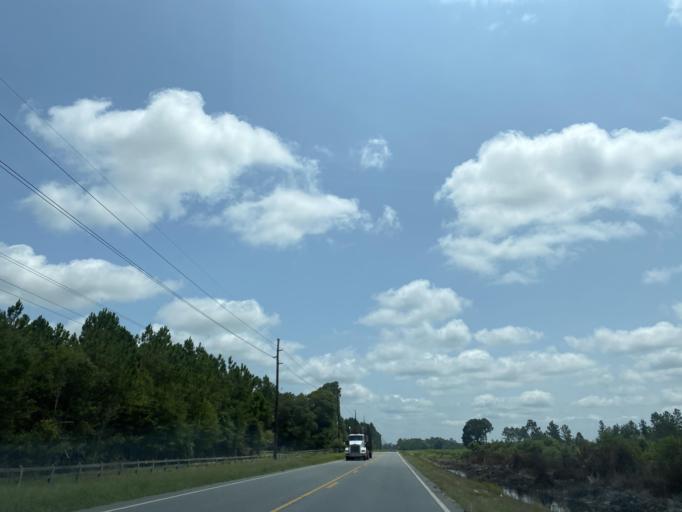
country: US
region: Georgia
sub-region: Jeff Davis County
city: Hazlehurst
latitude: 31.8361
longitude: -82.5796
